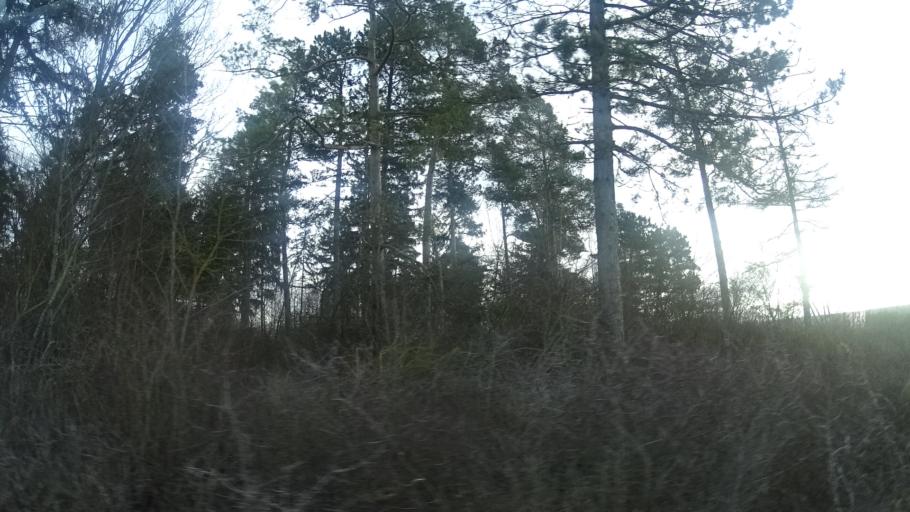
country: DE
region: Thuringia
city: Bad Blankenburg
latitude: 50.7267
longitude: 11.2371
